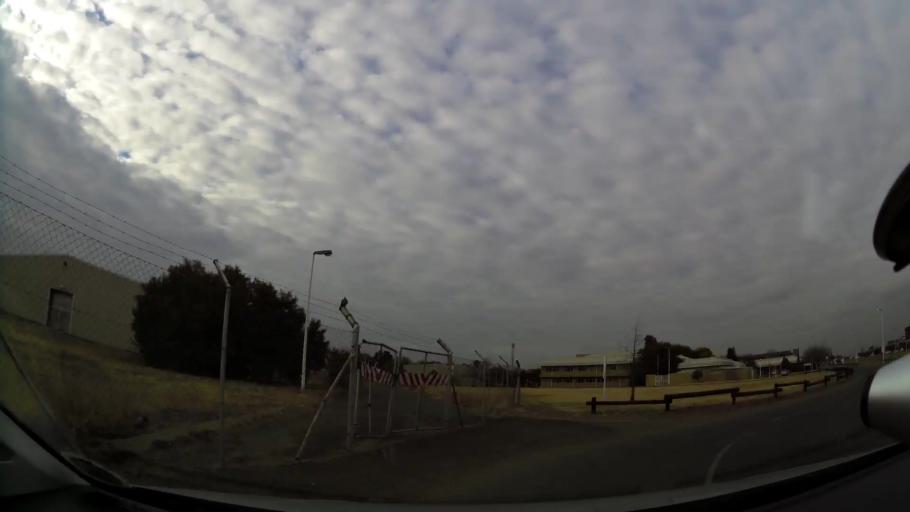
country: ZA
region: Orange Free State
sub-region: Mangaung Metropolitan Municipality
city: Bloemfontein
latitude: -29.1065
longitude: 26.1821
